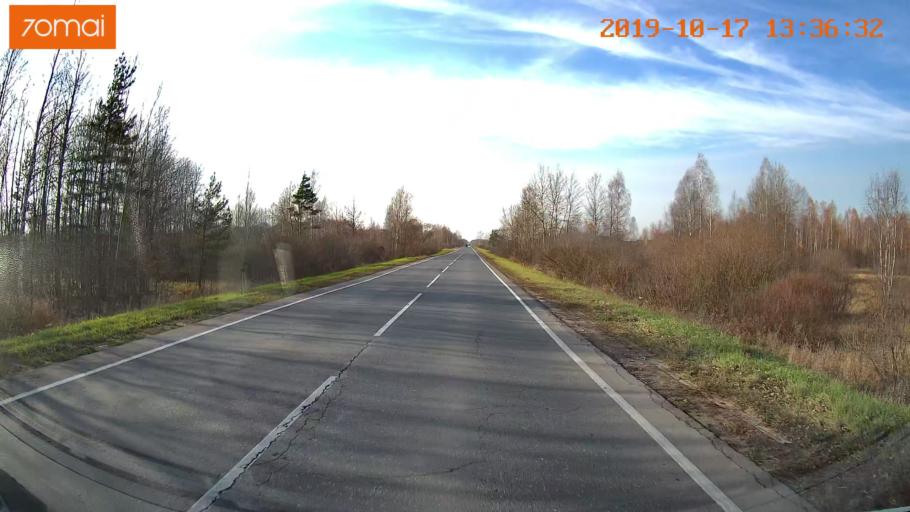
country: RU
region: Rjazan
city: Tuma
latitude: 55.1395
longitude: 40.6615
